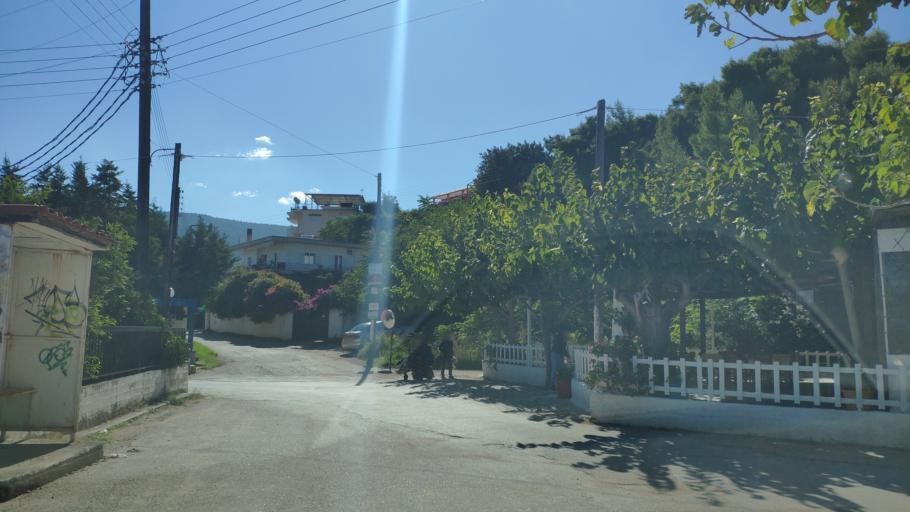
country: GR
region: Peloponnese
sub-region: Nomos Korinthias
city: Loutra Oraias Elenis
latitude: 37.8470
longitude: 22.9995
